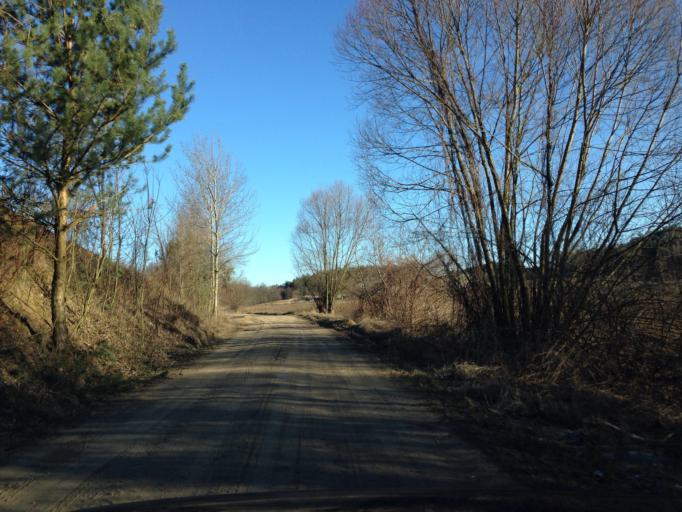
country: PL
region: Kujawsko-Pomorskie
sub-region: Powiat brodnicki
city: Brzozie
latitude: 53.3055
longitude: 19.6563
